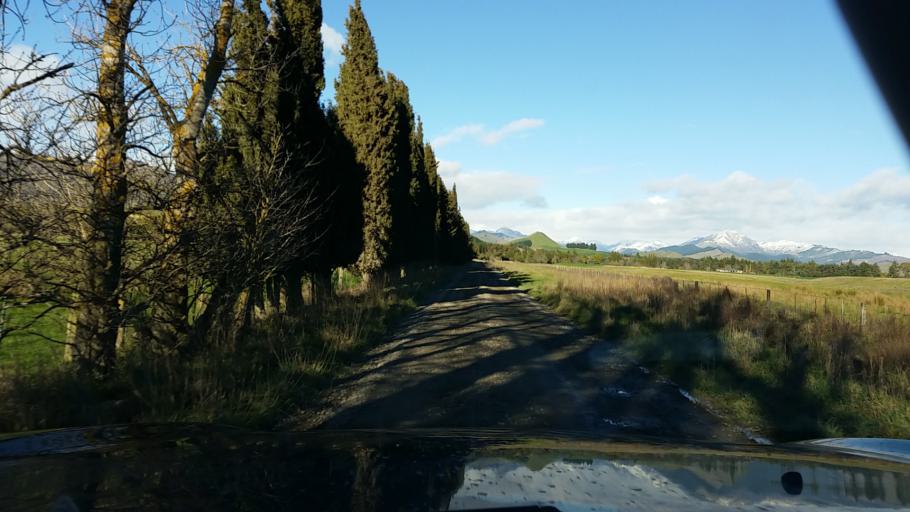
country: NZ
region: Marlborough
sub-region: Marlborough District
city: Blenheim
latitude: -41.6129
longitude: 173.6879
